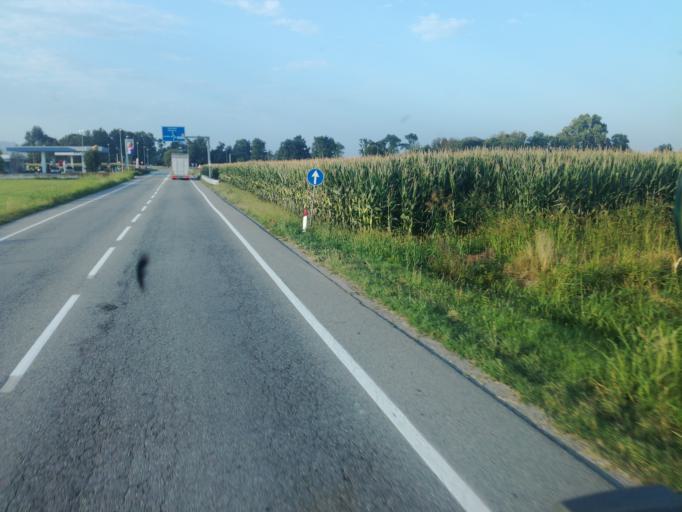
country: IT
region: Piedmont
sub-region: Provincia di Torino
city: Osasco
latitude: 44.8483
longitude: 7.3369
